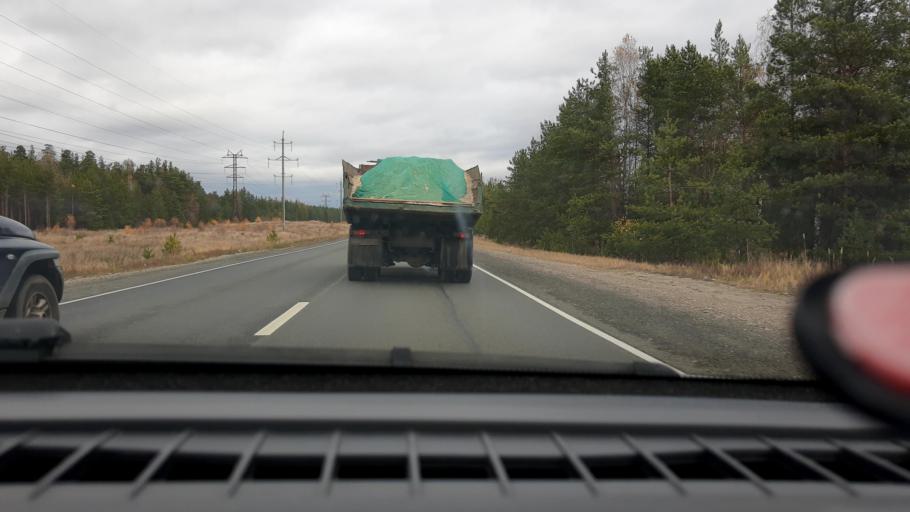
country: RU
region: Nizjnij Novgorod
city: Lukino
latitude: 56.3912
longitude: 43.6424
